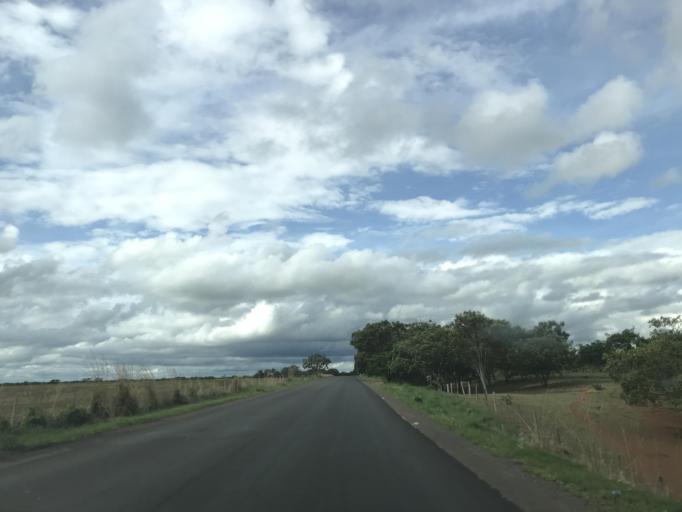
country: BR
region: Goias
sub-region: Bela Vista De Goias
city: Bela Vista de Goias
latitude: -16.9927
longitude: -48.6696
